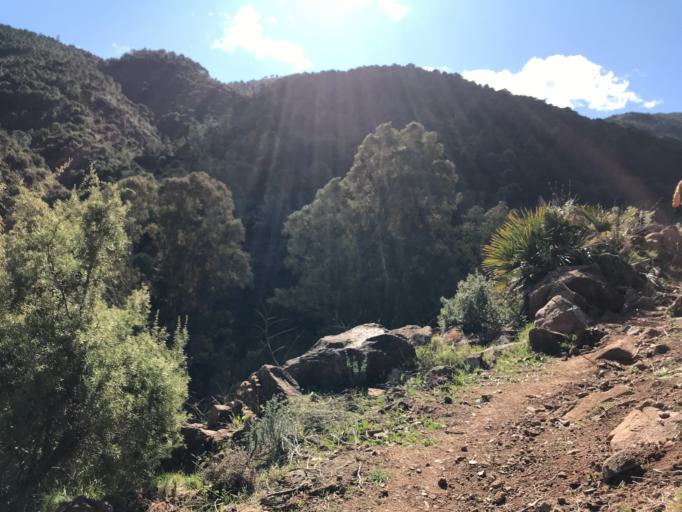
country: ES
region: Andalusia
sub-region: Provincia de Malaga
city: Tolox
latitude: 36.6714
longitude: -4.9218
